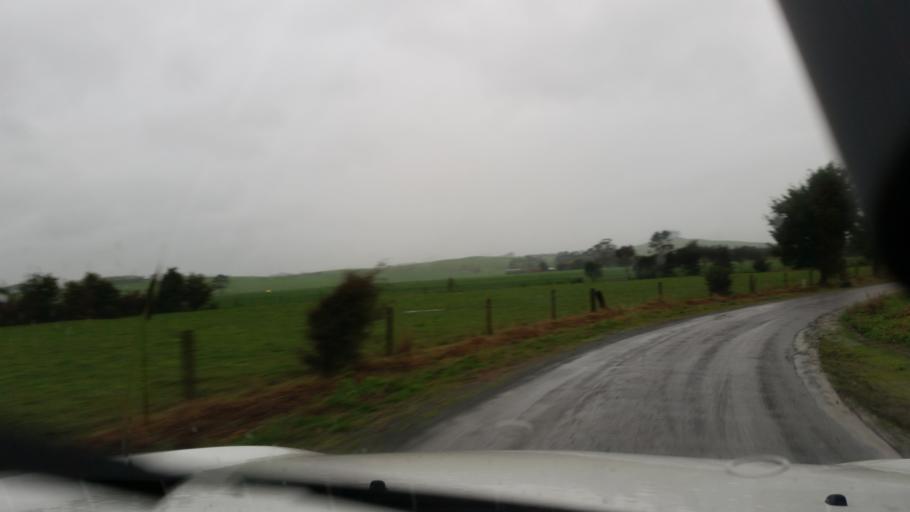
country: NZ
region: Northland
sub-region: Whangarei
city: Maungatapere
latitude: -35.7442
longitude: 174.0830
